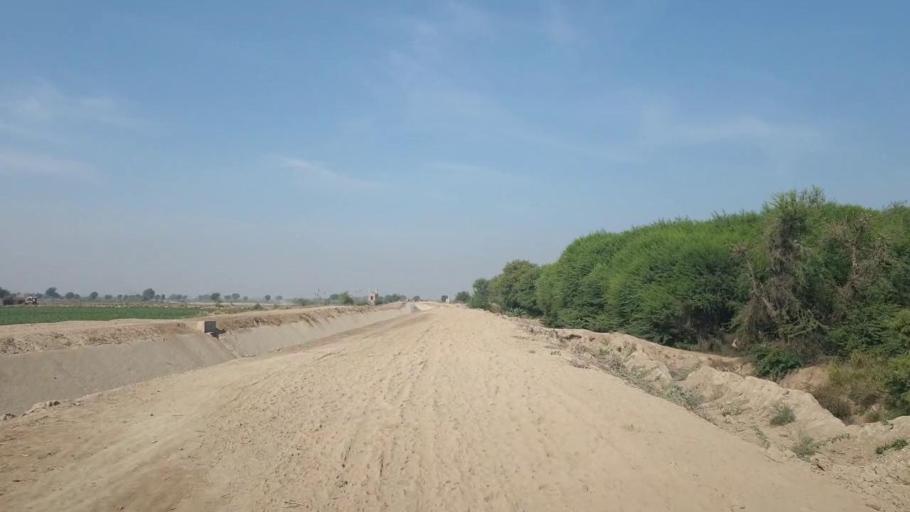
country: PK
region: Sindh
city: Matiari
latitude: 25.6843
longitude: 68.3351
